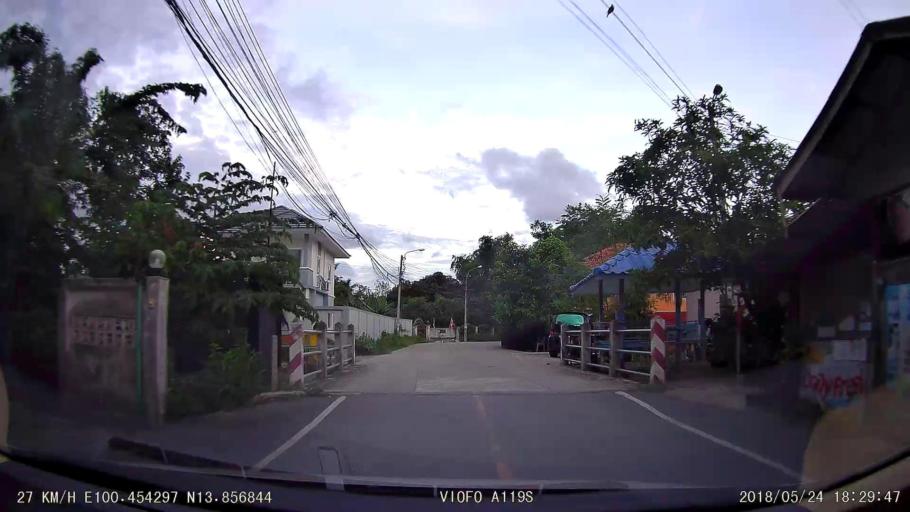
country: TH
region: Nonthaburi
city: Bang Kruai
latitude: 13.8572
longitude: 100.4541
